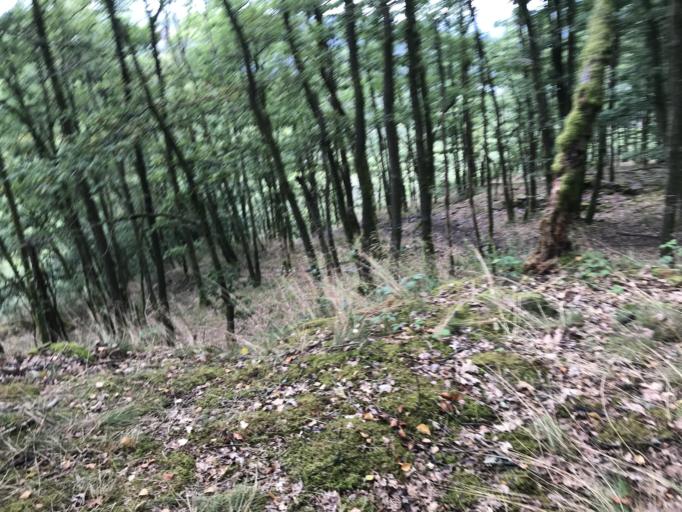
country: FR
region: Champagne-Ardenne
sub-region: Departement des Ardennes
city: Montherme
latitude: 49.8915
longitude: 4.7530
